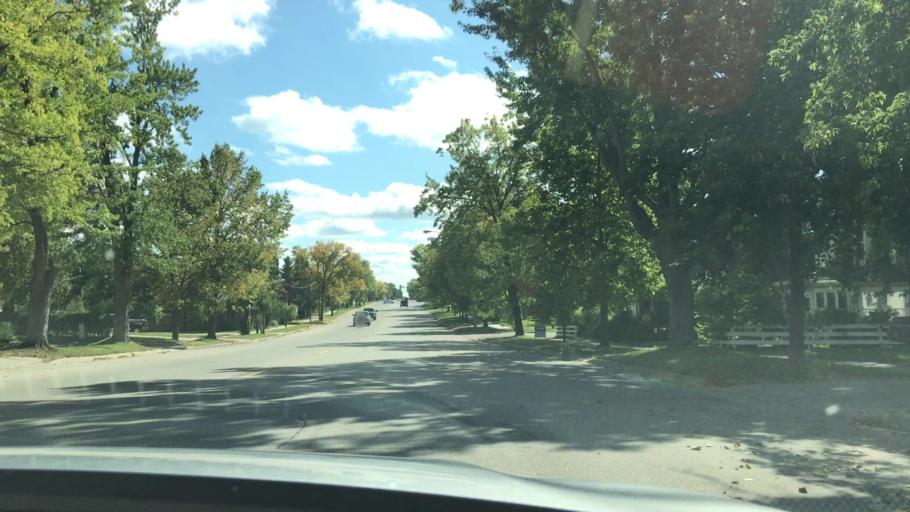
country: US
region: Minnesota
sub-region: Hubbard County
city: Park Rapids
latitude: 46.9251
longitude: -95.0585
